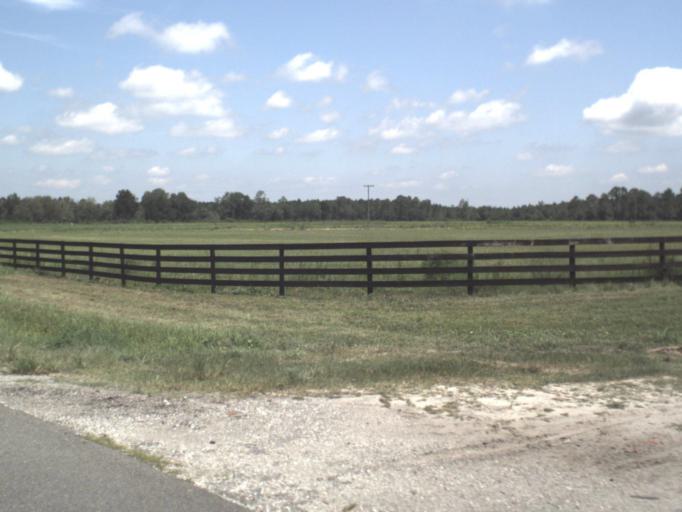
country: US
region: Florida
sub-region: Clay County
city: Green Cove Springs
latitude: 29.9800
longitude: -81.5537
